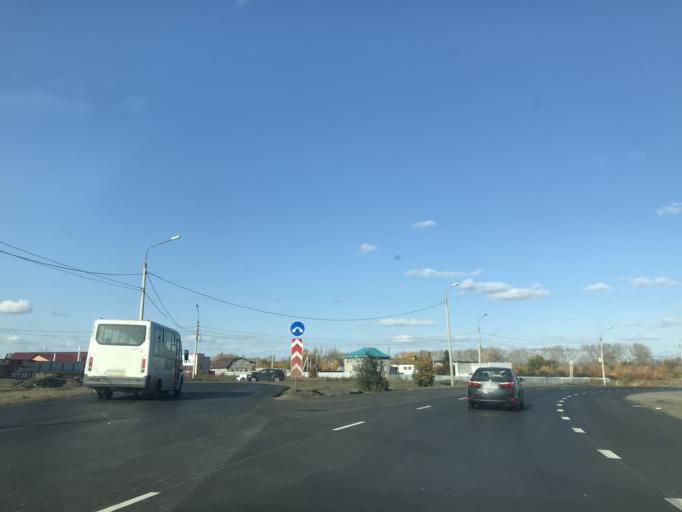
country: RU
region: Chelyabinsk
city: Roshchino
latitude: 55.2298
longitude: 61.2874
